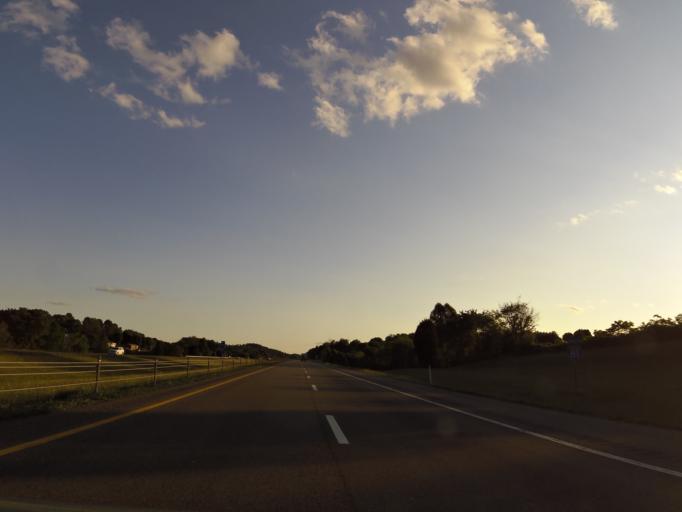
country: US
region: Tennessee
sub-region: Sullivan County
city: Blountville
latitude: 36.5276
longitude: -82.3955
